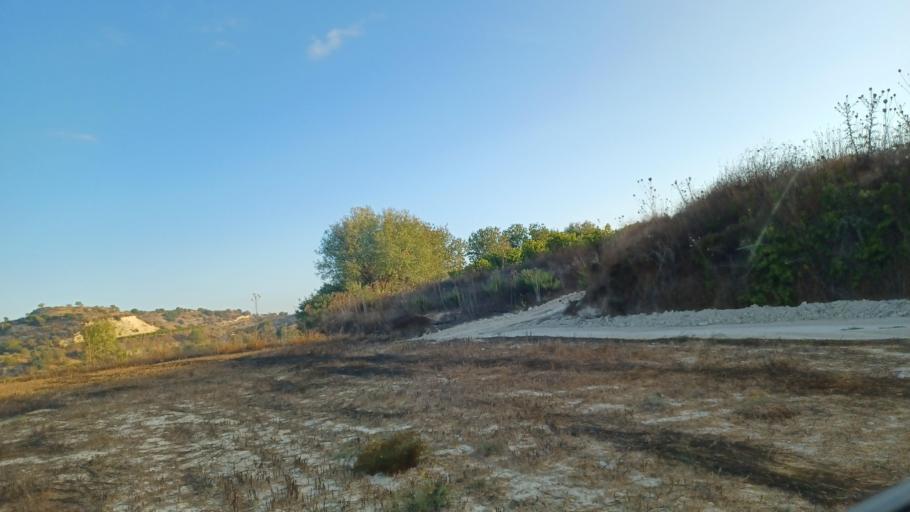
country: CY
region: Pafos
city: Mesogi
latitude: 34.8334
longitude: 32.5259
